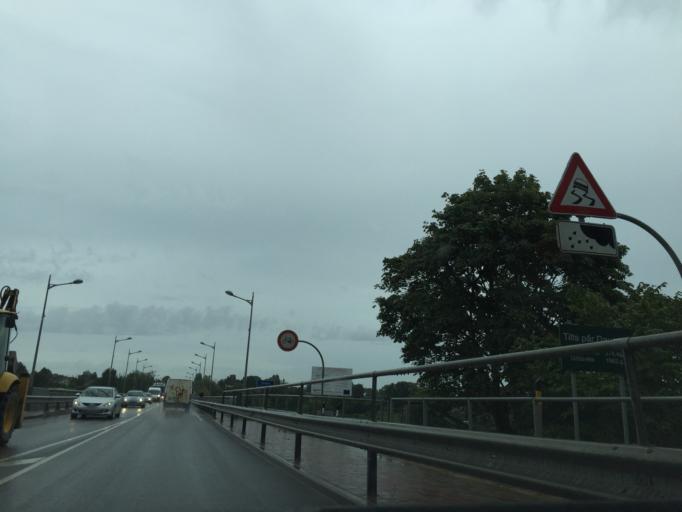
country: LV
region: Jekabpils Rajons
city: Jekabpils
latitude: 56.4981
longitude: 25.8785
